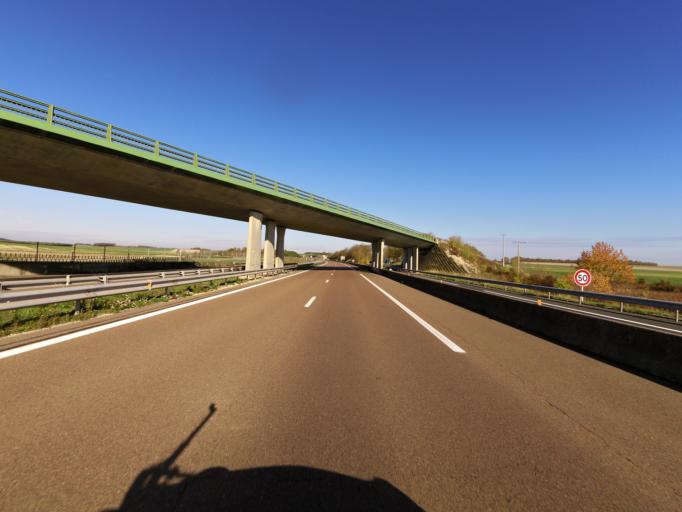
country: FR
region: Champagne-Ardenne
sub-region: Departement de la Marne
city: Compertrix
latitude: 48.8829
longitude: 4.2903
